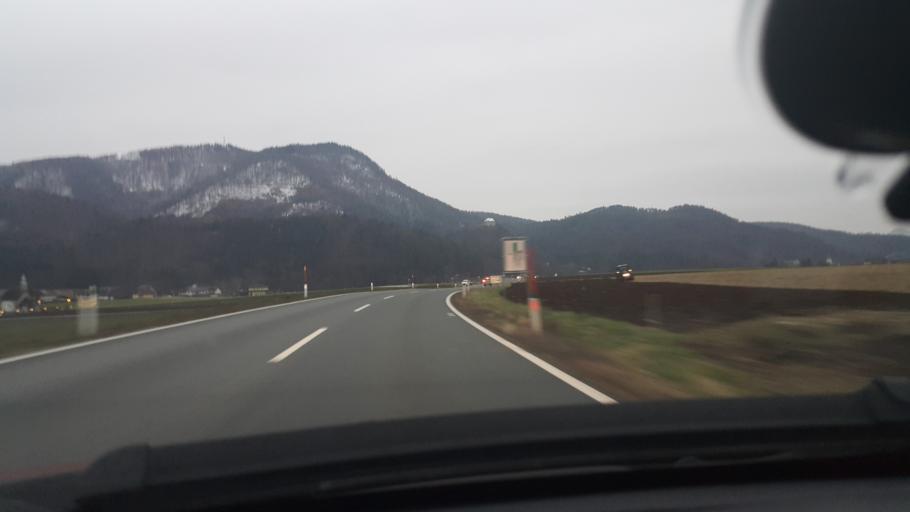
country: AT
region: Carinthia
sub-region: Politischer Bezirk Volkermarkt
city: Ruden
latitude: 46.6750
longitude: 14.7664
